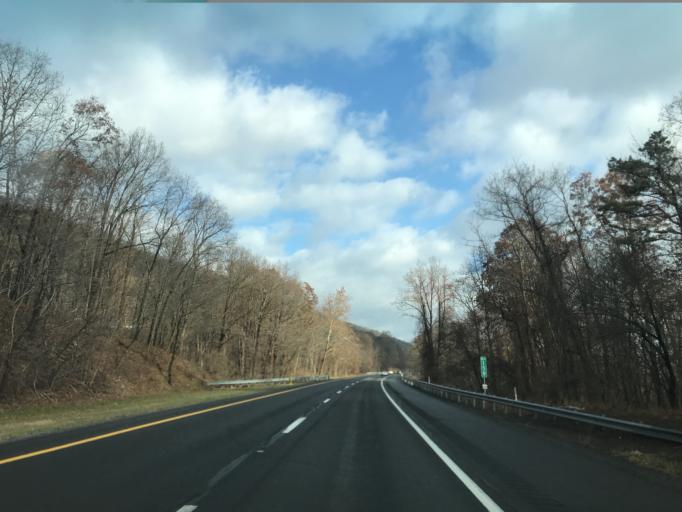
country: US
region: Maryland
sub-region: Washington County
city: Hancock
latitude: 39.8420
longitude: -78.2754
